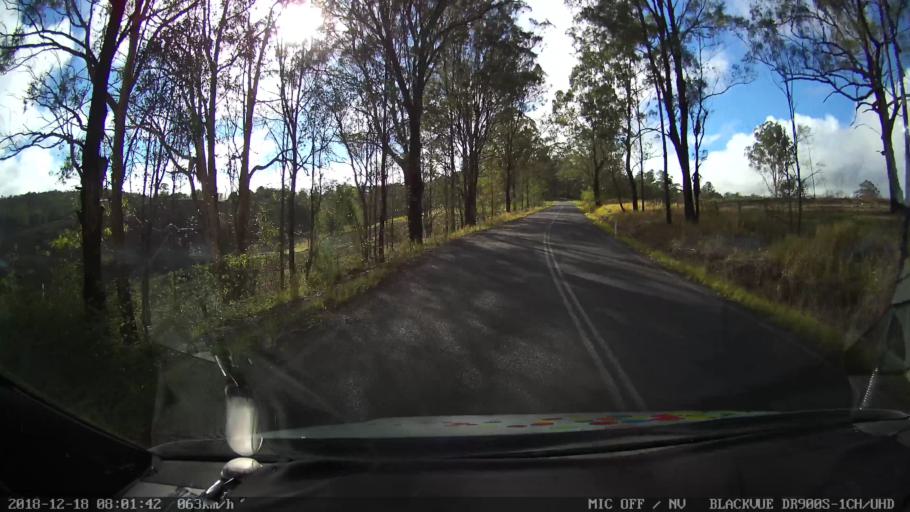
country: AU
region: New South Wales
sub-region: Kyogle
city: Kyogle
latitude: -28.3897
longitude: 152.6260
